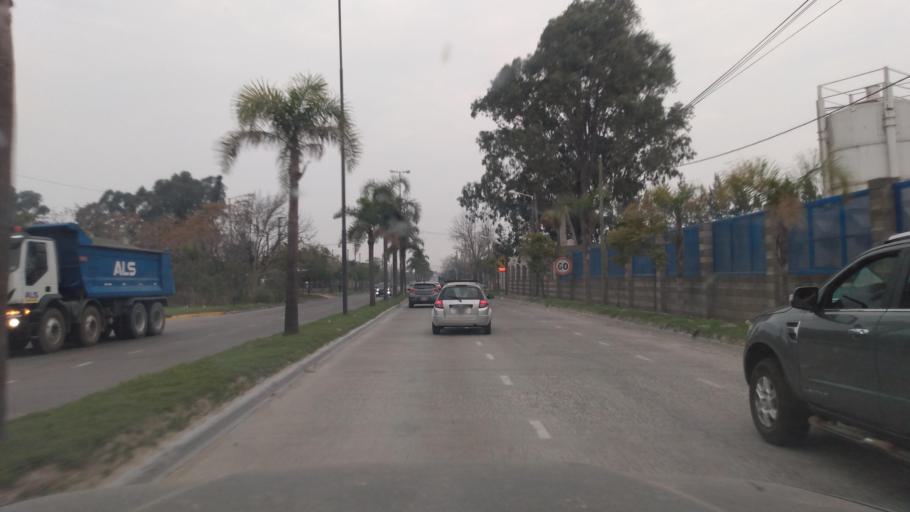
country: AR
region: Buenos Aires
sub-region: Partido de Tigre
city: Tigre
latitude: -34.4634
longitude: -58.5952
